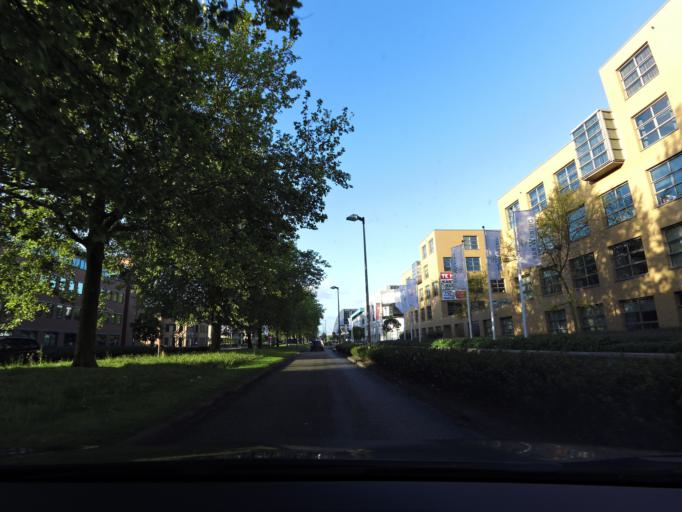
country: NL
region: South Holland
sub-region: Gemeente Rotterdam
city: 's-Gravenland
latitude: 51.9108
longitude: 4.5461
